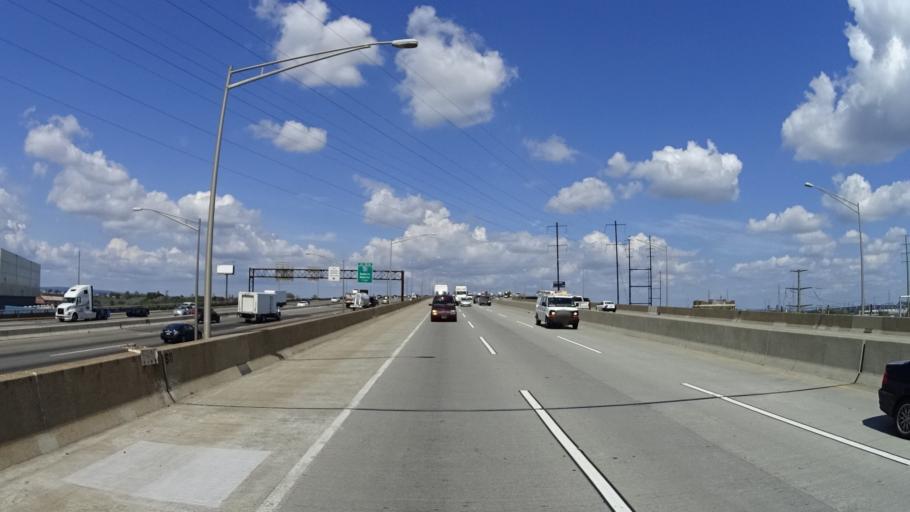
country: US
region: New Jersey
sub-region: Hudson County
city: Harrison
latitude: 40.7372
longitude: -74.1236
